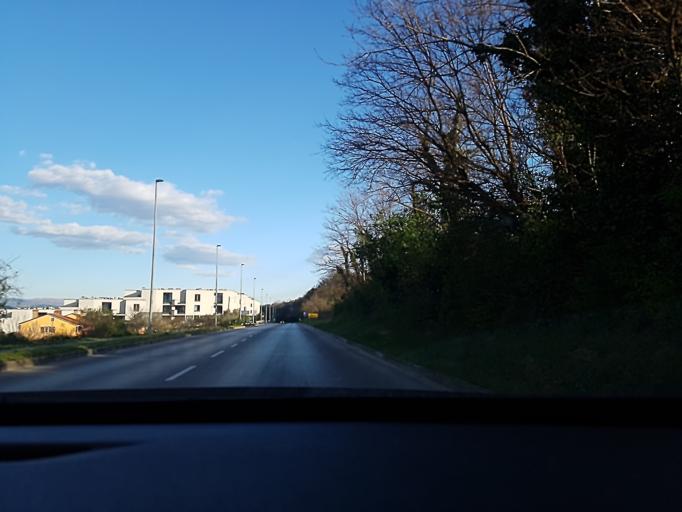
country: SI
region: Koper-Capodistria
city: Koper
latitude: 45.5419
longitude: 13.6975
